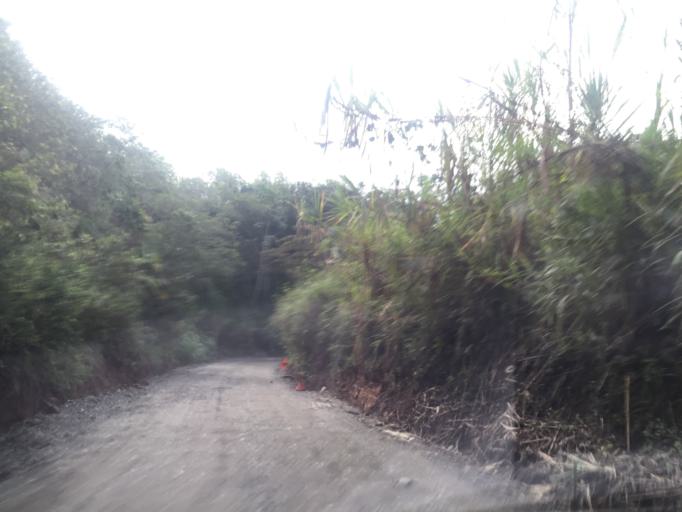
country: CO
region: Quindio
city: La Tebaida
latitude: 4.4638
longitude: -75.8059
